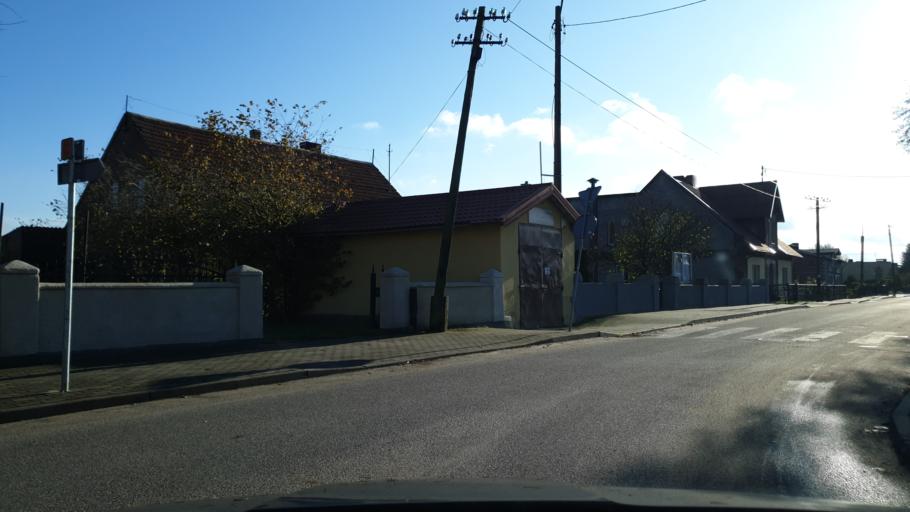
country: PL
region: Pomeranian Voivodeship
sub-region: Powiat pucki
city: Gniezdzewo
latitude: 54.7596
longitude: 18.3999
